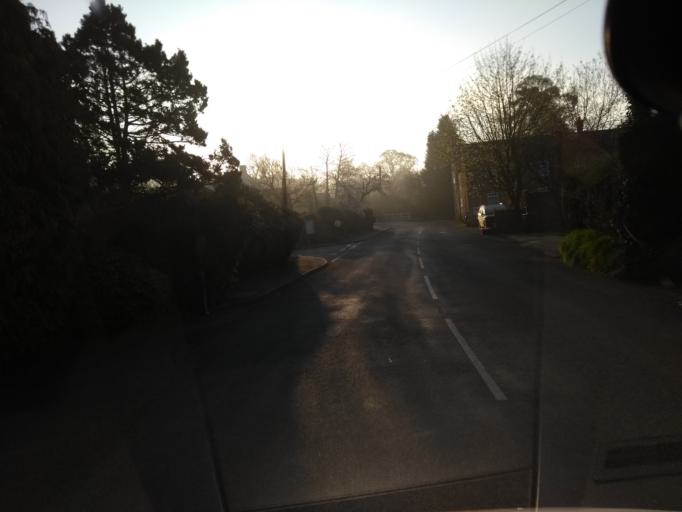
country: GB
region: England
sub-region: Somerset
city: Crewkerne
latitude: 50.8415
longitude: -2.8300
